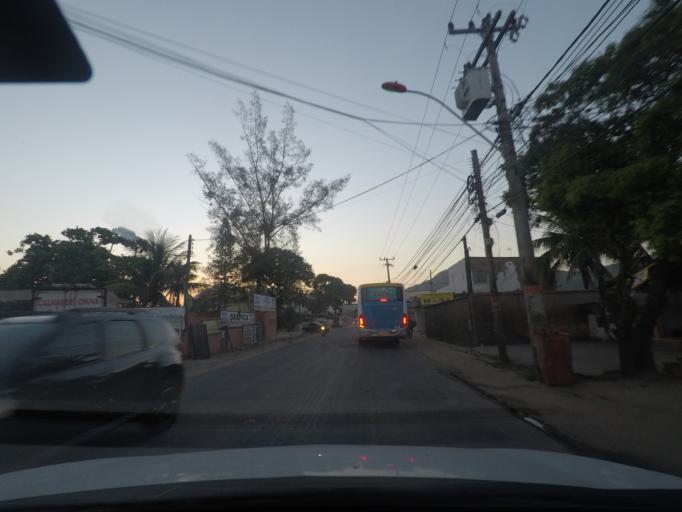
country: BR
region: Rio de Janeiro
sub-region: Niteroi
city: Niteroi
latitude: -22.9622
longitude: -42.9891
